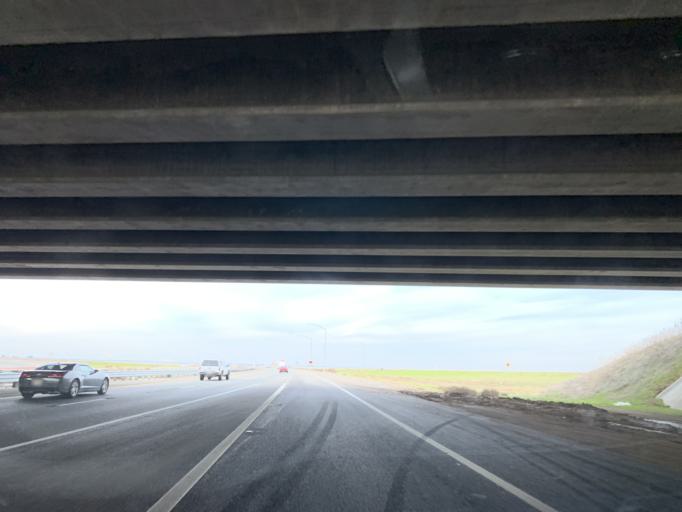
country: US
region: California
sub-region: Sacramento County
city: Elverta
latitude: 38.7503
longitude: -121.5403
